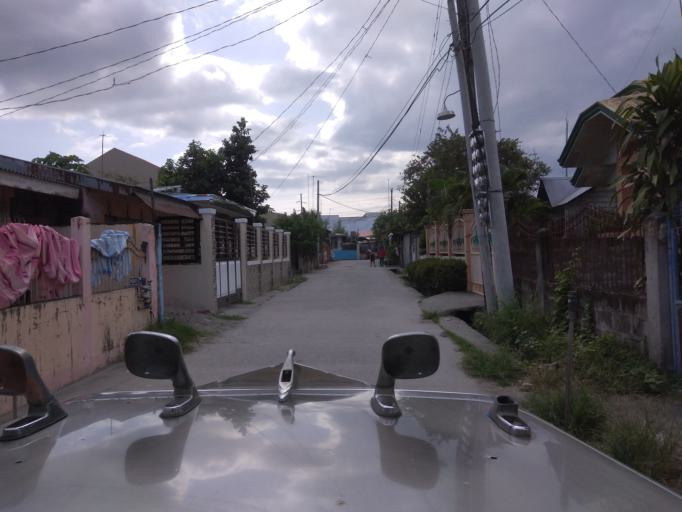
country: PH
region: Central Luzon
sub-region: Province of Pampanga
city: Pandacaqui
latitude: 15.1820
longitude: 120.6472
